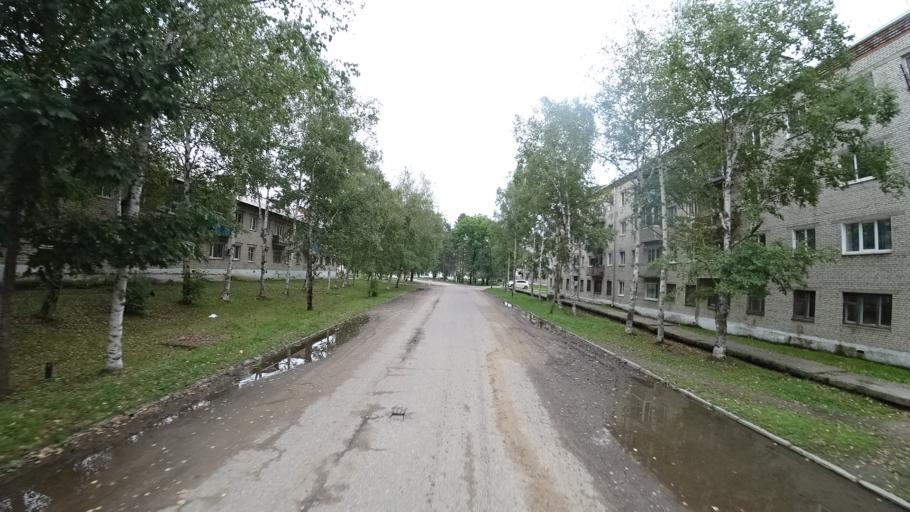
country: RU
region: Primorskiy
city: Rettikhovka
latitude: 44.1684
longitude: 132.7755
